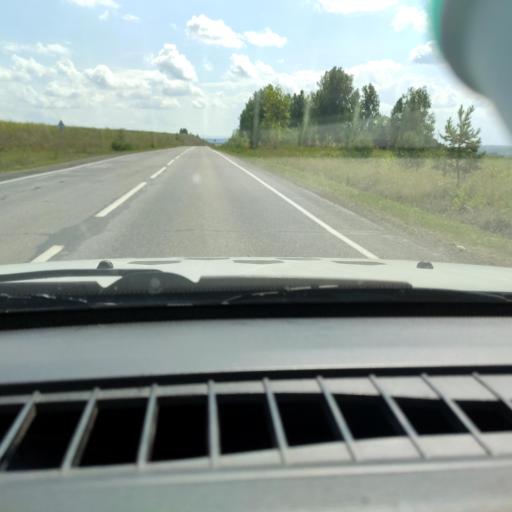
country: RU
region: Bashkortostan
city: Verkhniye Kigi
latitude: 55.3437
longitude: 58.6854
